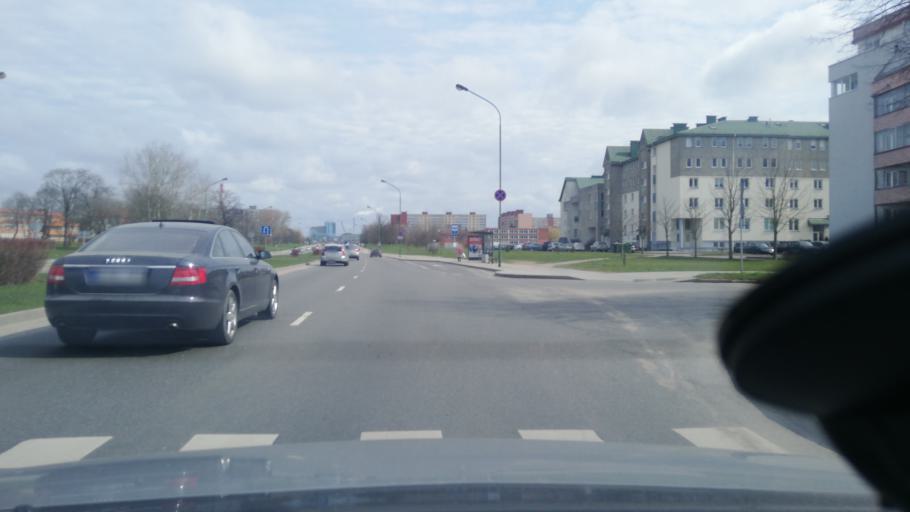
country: LT
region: Klaipedos apskritis
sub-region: Klaipeda
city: Klaipeda
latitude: 55.6745
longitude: 21.1804
